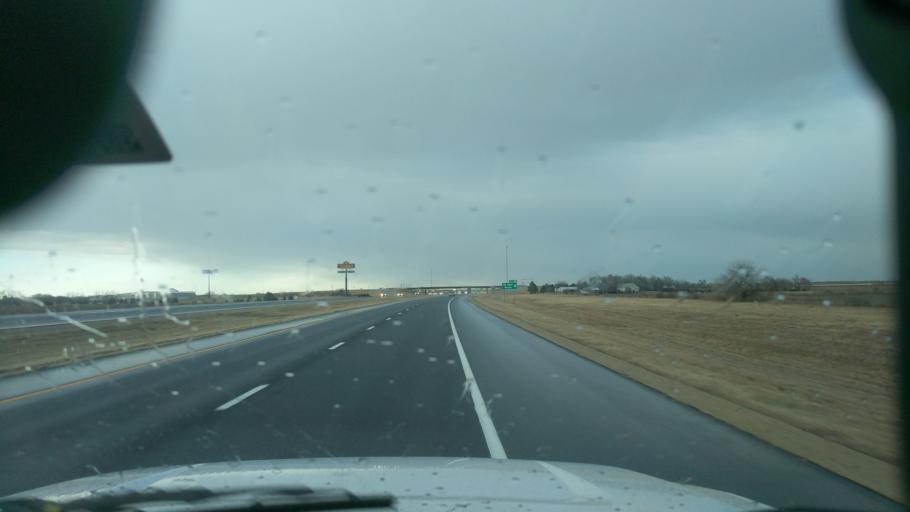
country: US
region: Kansas
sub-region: Harvey County
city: Newton
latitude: 37.9935
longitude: -97.3280
